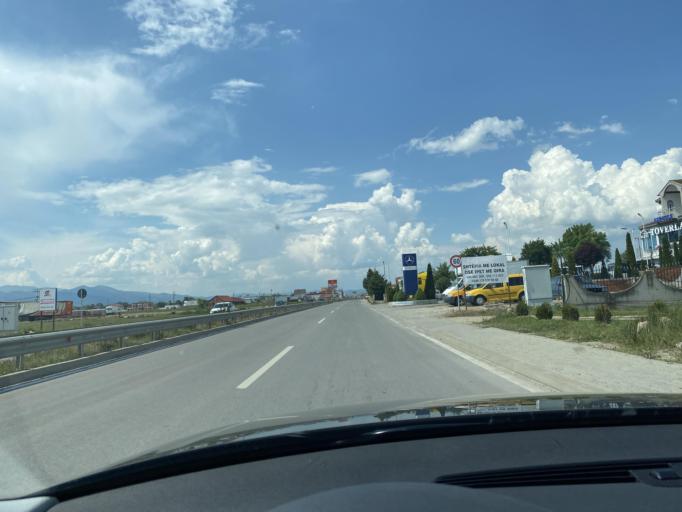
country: XK
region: Pristina
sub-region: Podujevo
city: Podujeva
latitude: 42.8740
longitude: 21.1822
